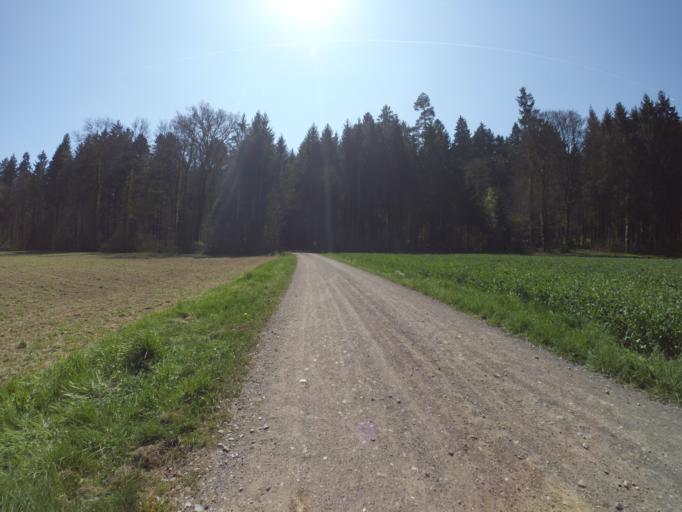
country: CH
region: Thurgau
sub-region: Frauenfeld District
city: Diessenhofen
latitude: 47.6486
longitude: 8.7425
